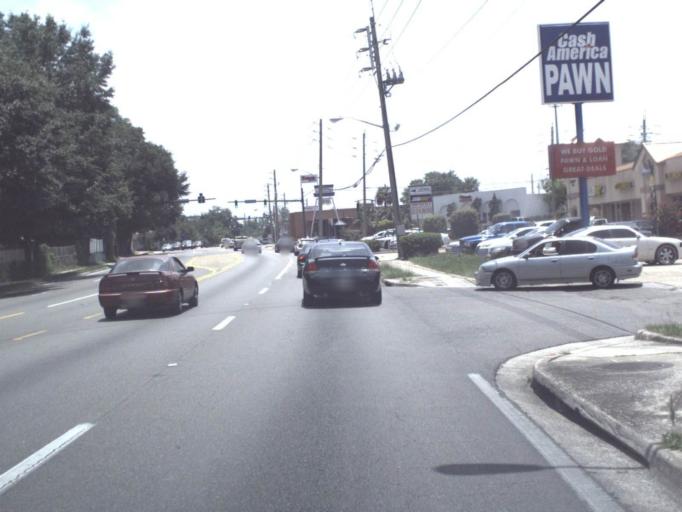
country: US
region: Florida
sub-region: Duval County
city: Jacksonville
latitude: 30.3939
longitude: -81.6819
